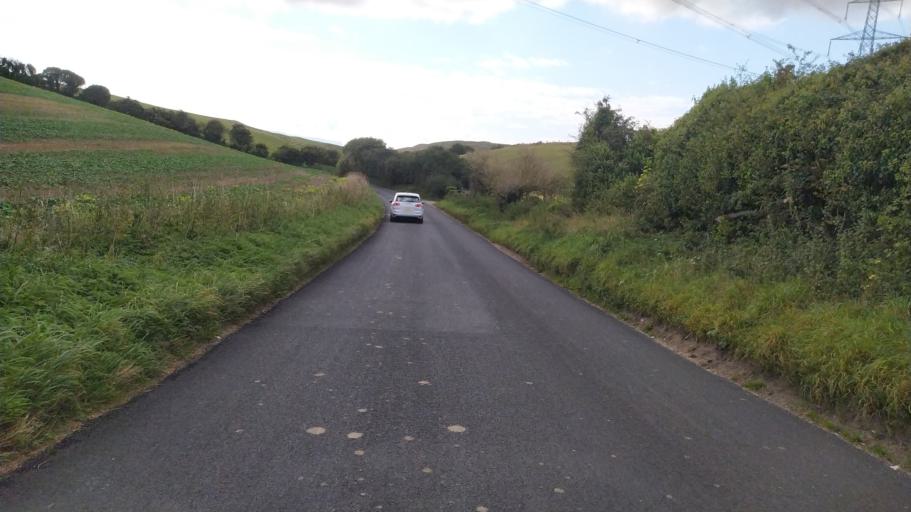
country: GB
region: England
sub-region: Dorset
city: Overcombe
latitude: 50.6616
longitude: -2.4286
